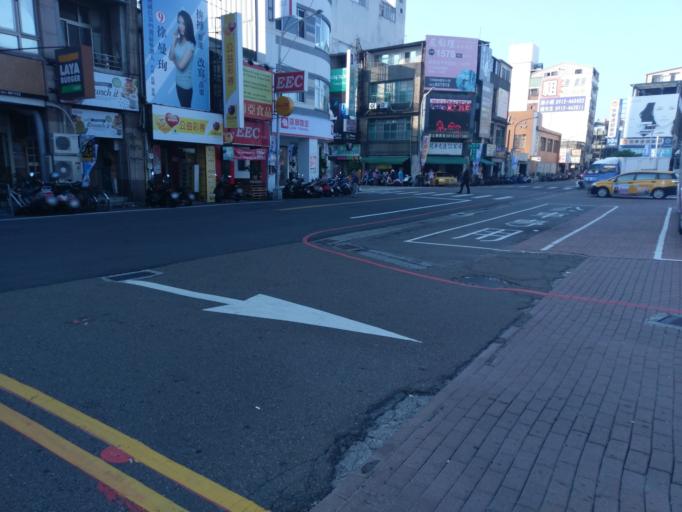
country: TW
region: Taiwan
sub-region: Miaoli
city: Miaoli
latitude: 24.6862
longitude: 120.8801
